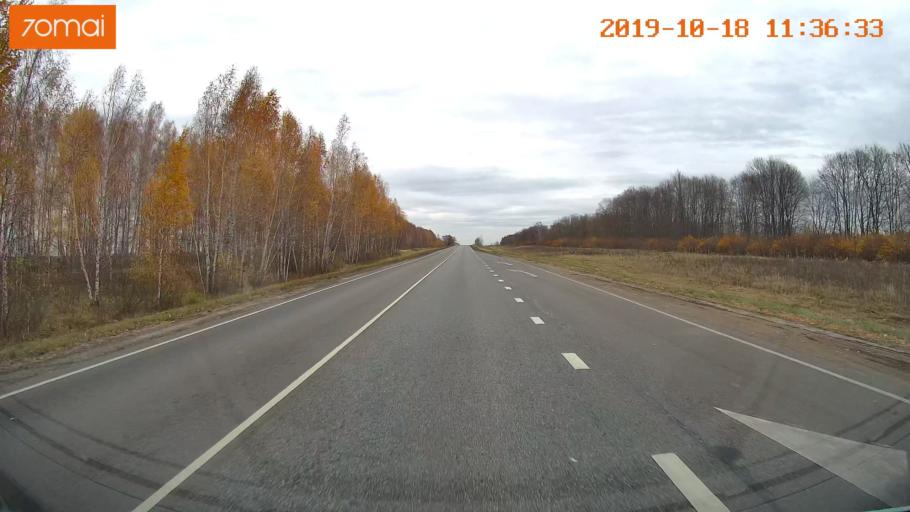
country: RU
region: Rjazan
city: Oktyabr'skiy
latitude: 54.1421
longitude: 38.8091
